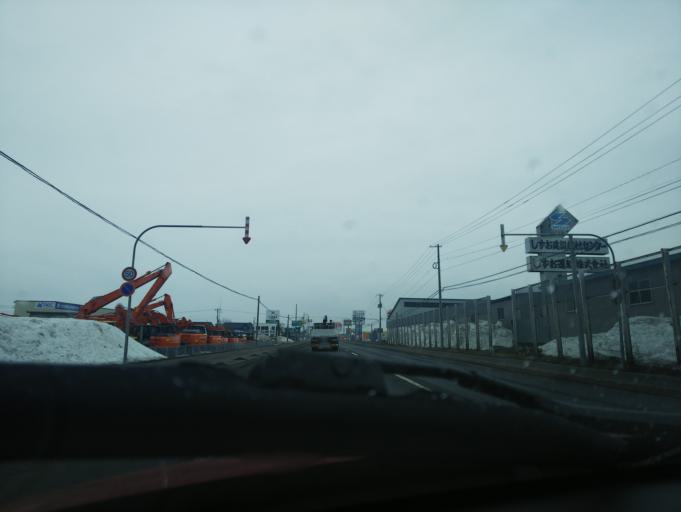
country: JP
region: Hokkaido
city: Nayoro
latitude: 44.1587
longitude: 142.3976
